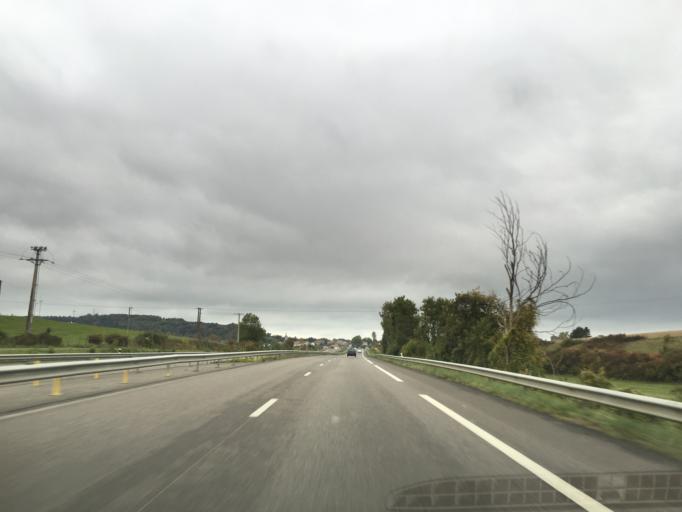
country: FR
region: Lorraine
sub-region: Departement de la Meuse
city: Vacon
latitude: 48.6971
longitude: 5.5427
